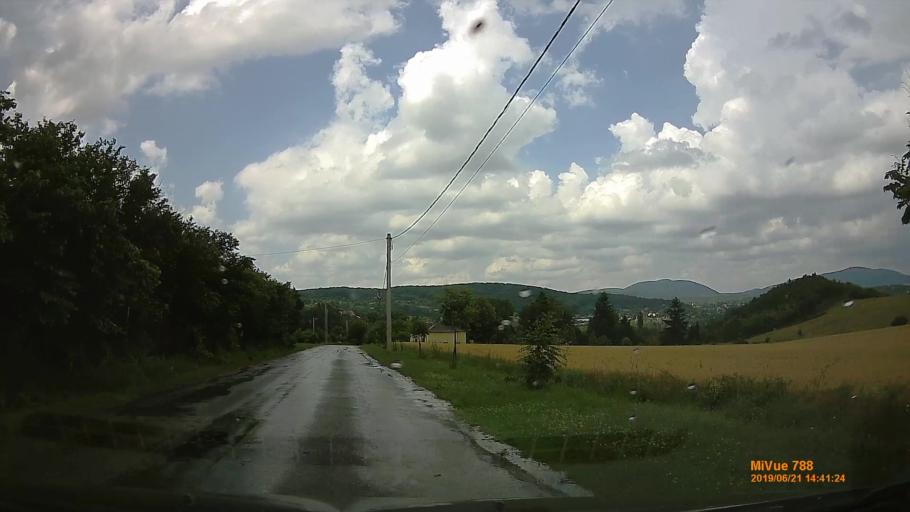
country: HU
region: Baranya
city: Hosszuheteny
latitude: 46.1155
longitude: 18.3121
